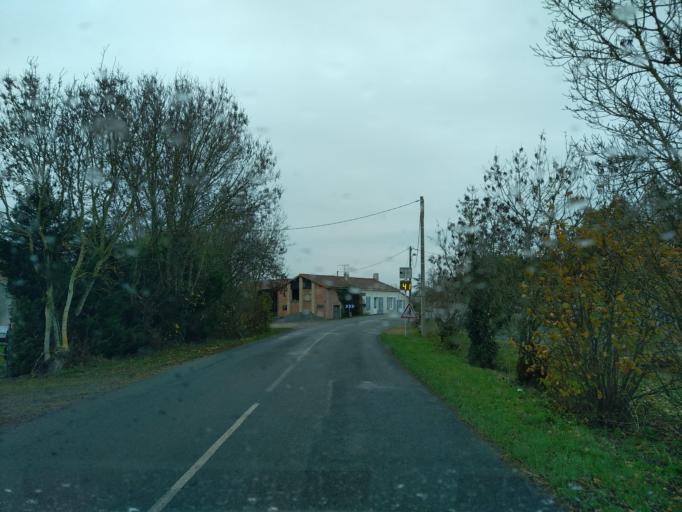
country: FR
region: Pays de la Loire
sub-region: Departement de la Vendee
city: Maillezais
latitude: 46.3221
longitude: -0.7870
